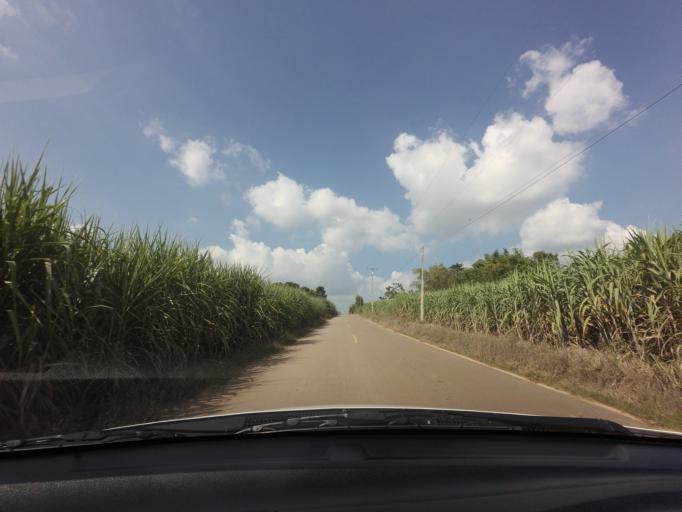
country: TH
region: Nakhon Ratchasima
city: Wang Nam Khiao
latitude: 14.5102
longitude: 101.6303
